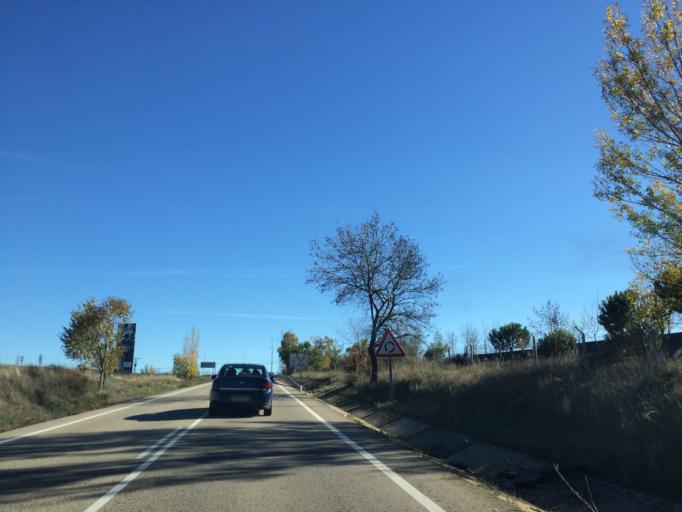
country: ES
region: Madrid
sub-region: Provincia de Madrid
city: Manzanares el Real
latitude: 40.7335
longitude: -3.7918
